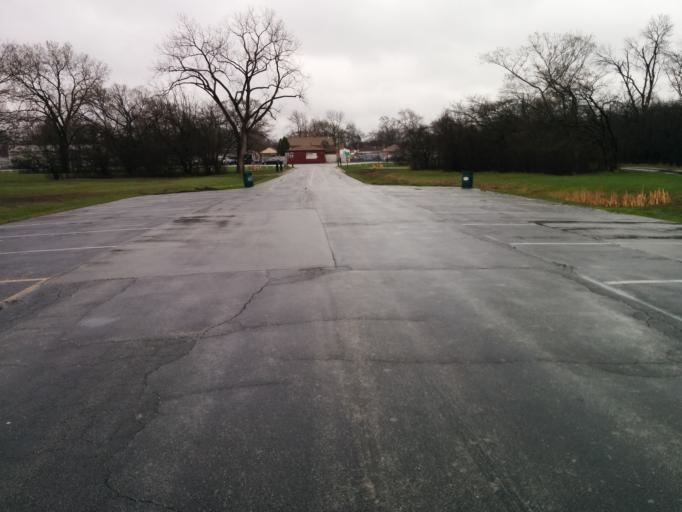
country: US
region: Illinois
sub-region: Cook County
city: Riverdale
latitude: 41.6307
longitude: -87.6430
